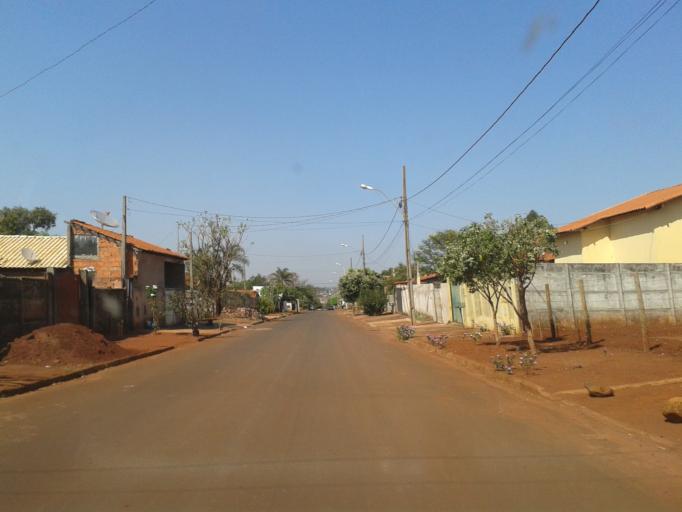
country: BR
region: Minas Gerais
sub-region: Ituiutaba
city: Ituiutaba
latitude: -18.9587
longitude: -49.4830
